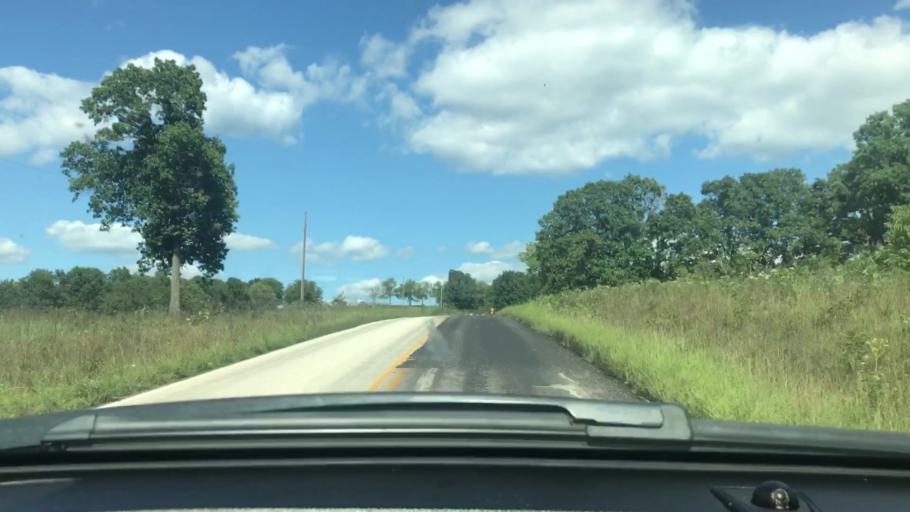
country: US
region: Missouri
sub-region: Wright County
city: Hartville
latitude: 37.3745
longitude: -92.3844
